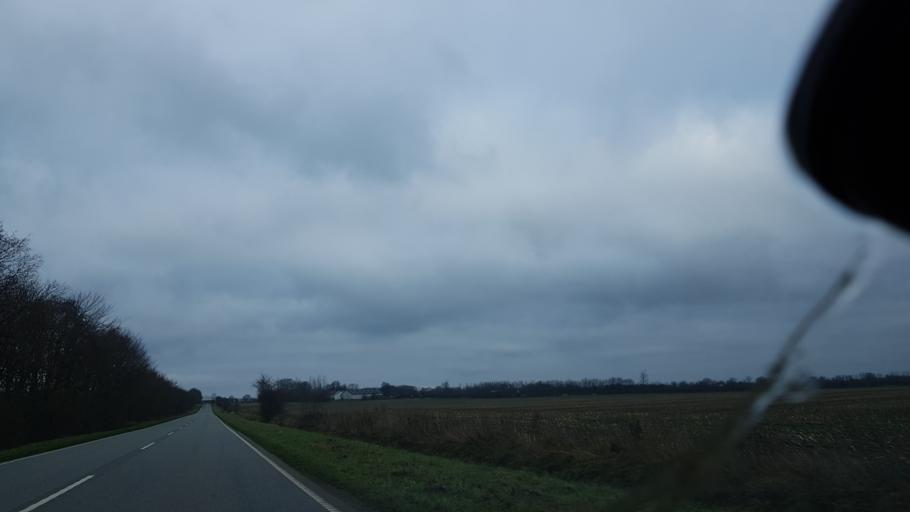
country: DK
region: South Denmark
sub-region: Haderslev Kommune
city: Vojens
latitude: 55.2356
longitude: 9.2145
